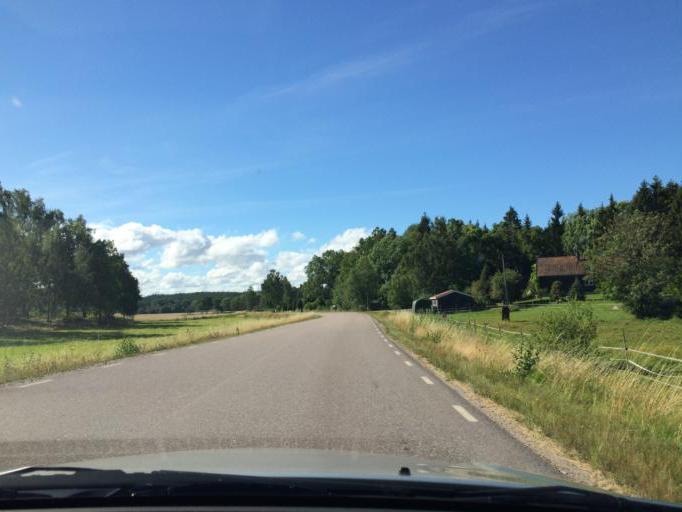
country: SE
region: Soedermanland
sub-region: Eskilstuna Kommun
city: Torshalla
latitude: 59.5180
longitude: 16.4372
